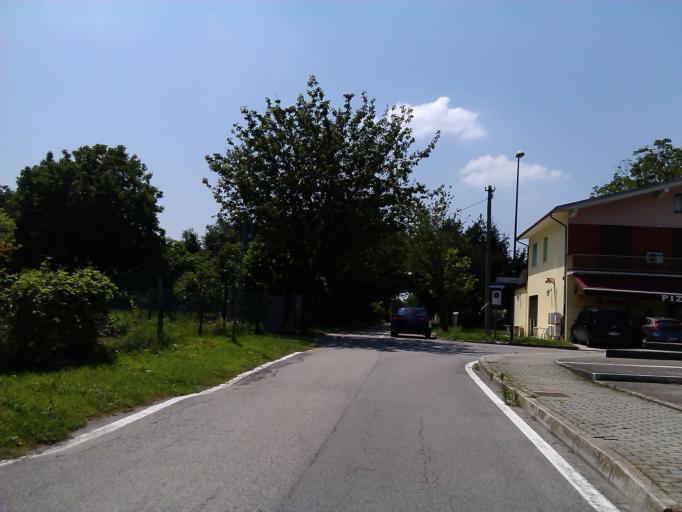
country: IT
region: Veneto
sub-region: Provincia di Venezia
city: Fornase
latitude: 45.4563
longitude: 12.1865
